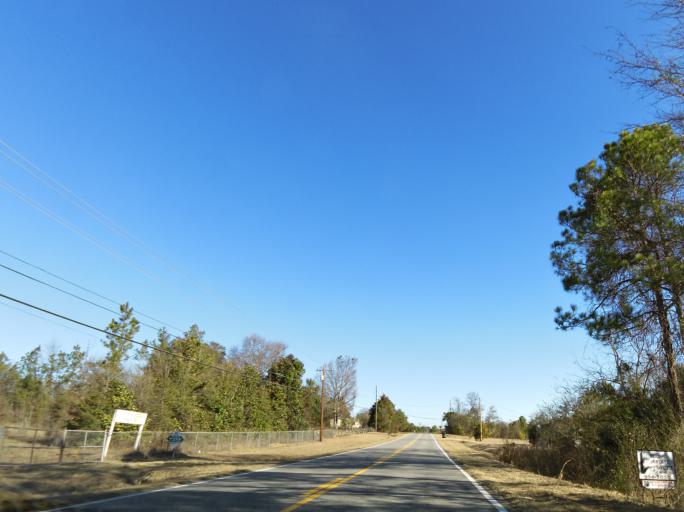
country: US
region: Georgia
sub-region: Bibb County
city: West Point
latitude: 32.7707
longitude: -83.7573
